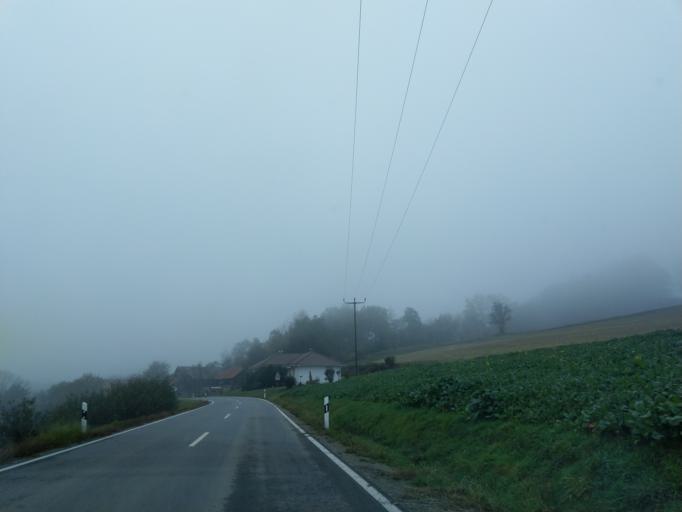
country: DE
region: Bavaria
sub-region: Lower Bavaria
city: Grattersdorf
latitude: 48.7906
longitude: 13.1557
